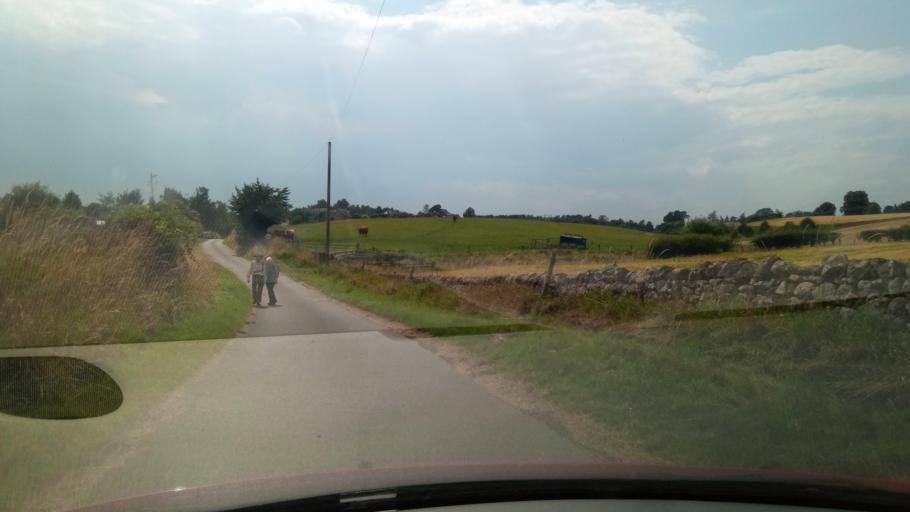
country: GB
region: Scotland
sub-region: The Scottish Borders
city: Kelso
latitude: 55.5718
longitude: -2.4728
